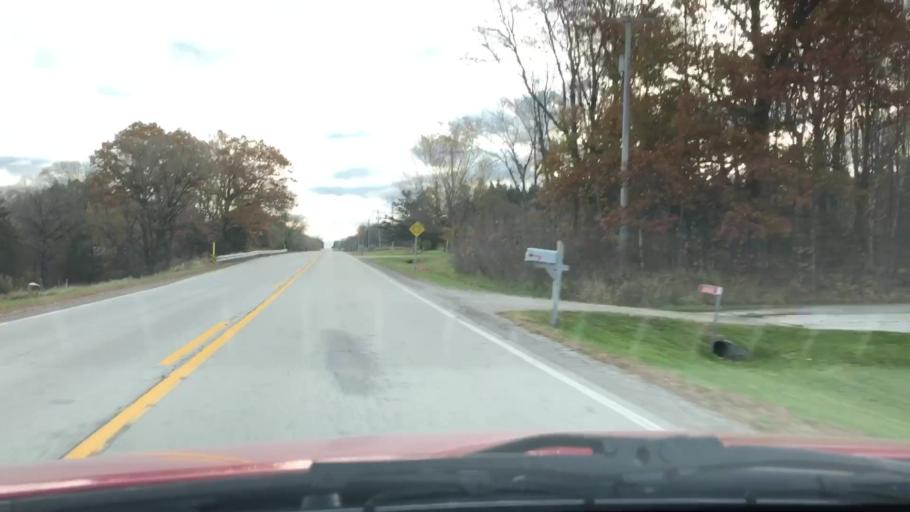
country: US
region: Wisconsin
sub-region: Brown County
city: Oneida
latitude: 44.4444
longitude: -88.2413
